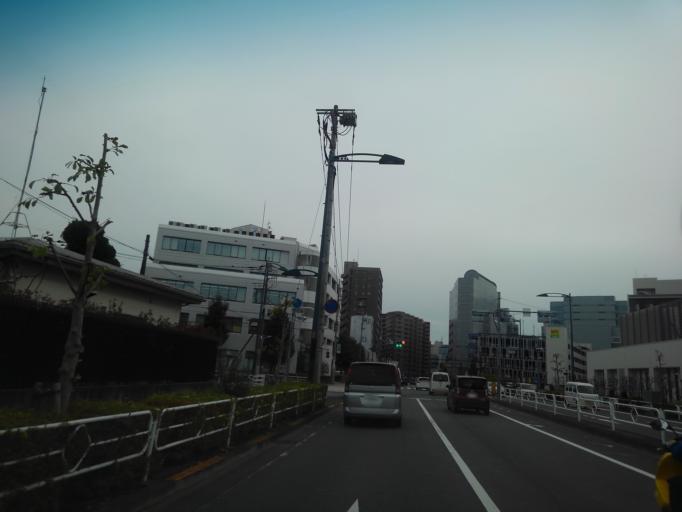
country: JP
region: Tokyo
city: Hino
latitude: 35.7051
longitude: 139.4137
